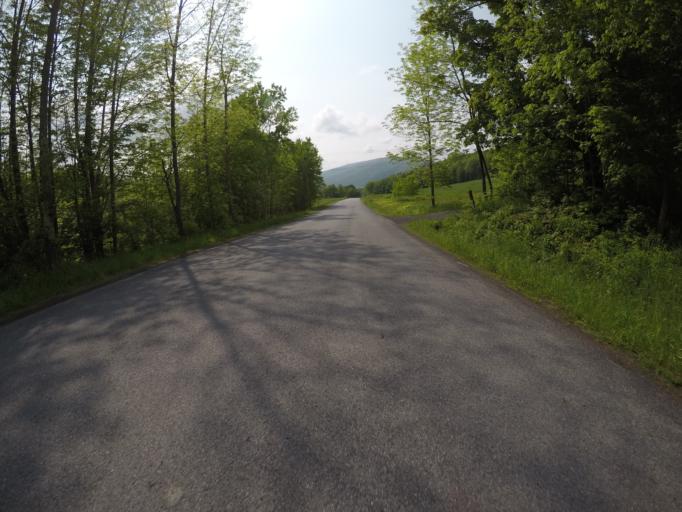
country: US
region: New York
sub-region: Delaware County
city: Stamford
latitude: 42.1655
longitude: -74.6668
